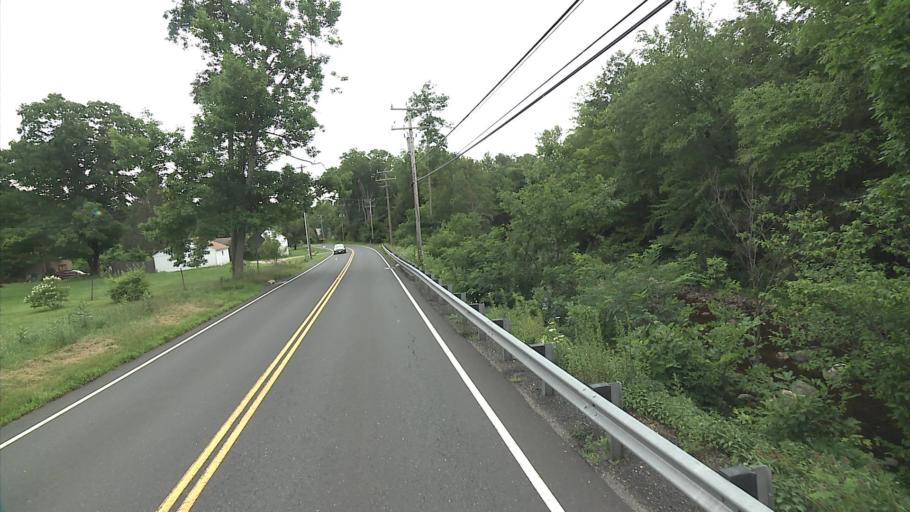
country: US
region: Connecticut
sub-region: Litchfield County
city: Winsted
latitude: 41.9842
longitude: -73.0454
